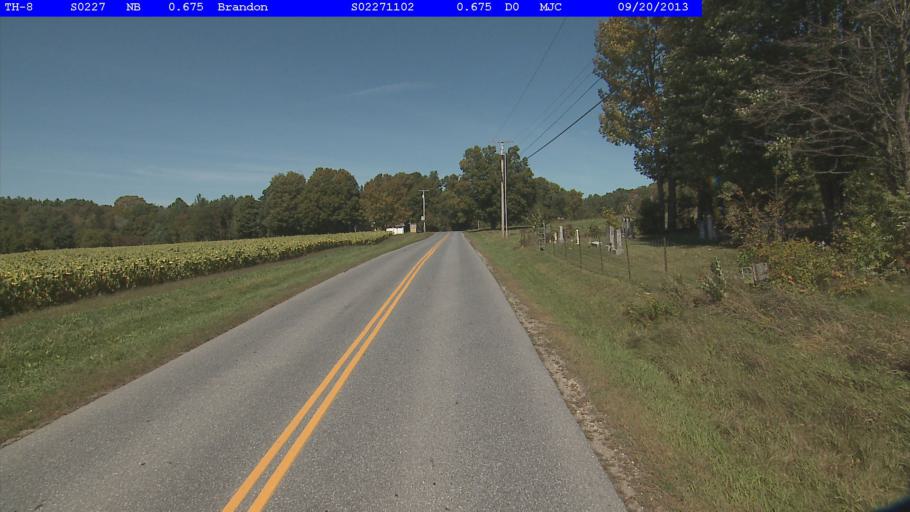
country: US
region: Vermont
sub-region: Rutland County
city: Brandon
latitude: 43.7841
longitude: -73.0532
